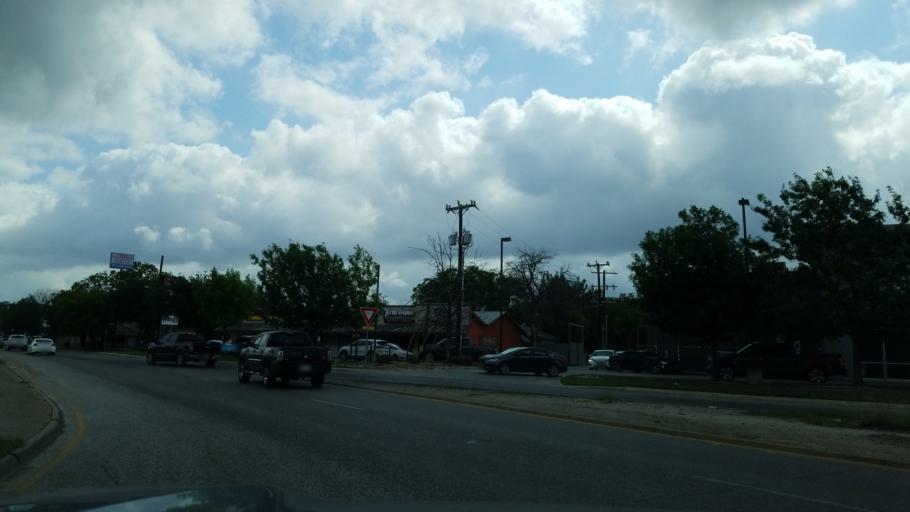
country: US
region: Texas
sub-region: Bexar County
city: San Antonio
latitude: 29.3571
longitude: -98.5251
